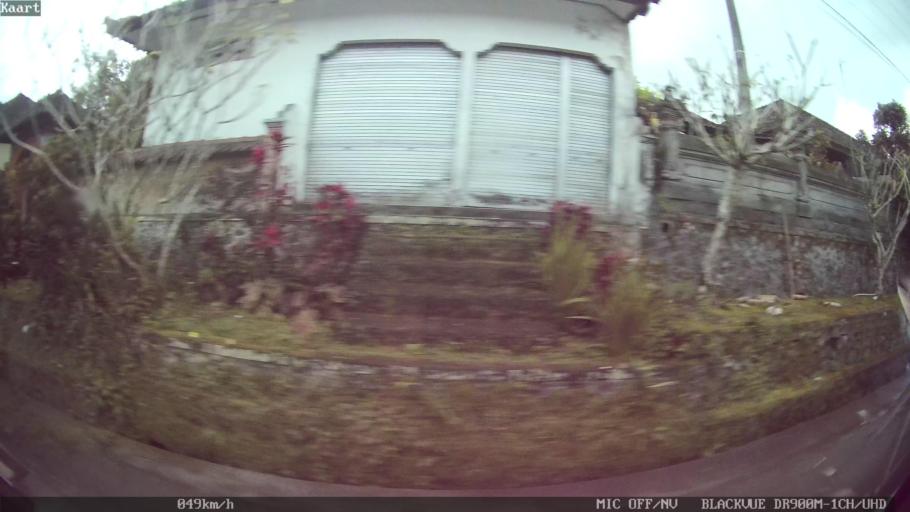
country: ID
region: Bali
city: Banjar Kubu
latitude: -8.4284
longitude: 115.4225
